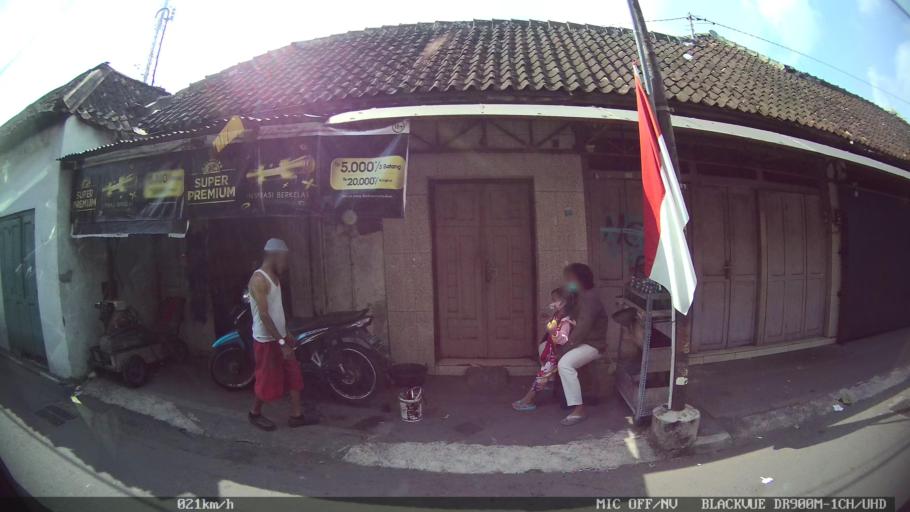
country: ID
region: Daerah Istimewa Yogyakarta
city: Yogyakarta
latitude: -7.8276
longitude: 110.3989
